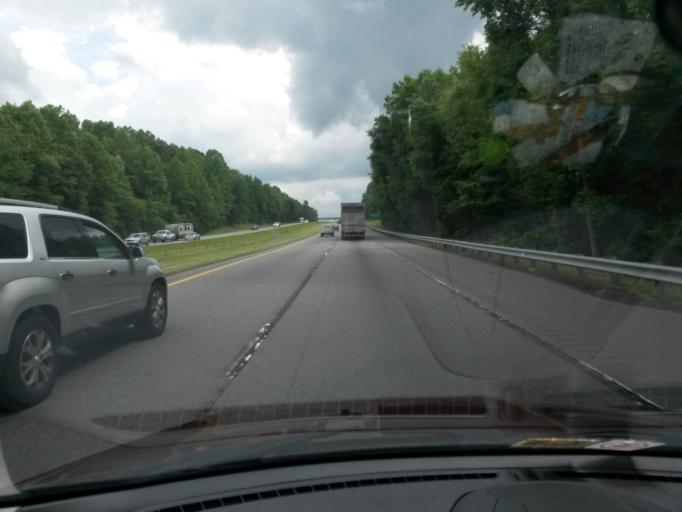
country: US
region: North Carolina
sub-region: Iredell County
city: Statesville
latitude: 35.9439
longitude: -80.8524
